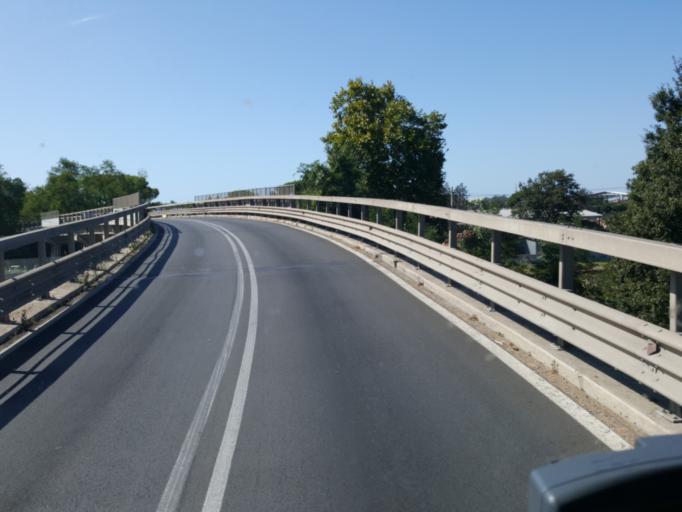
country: IT
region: Latium
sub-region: Citta metropolitana di Roma Capitale
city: Anzio
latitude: 41.5148
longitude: 12.6304
